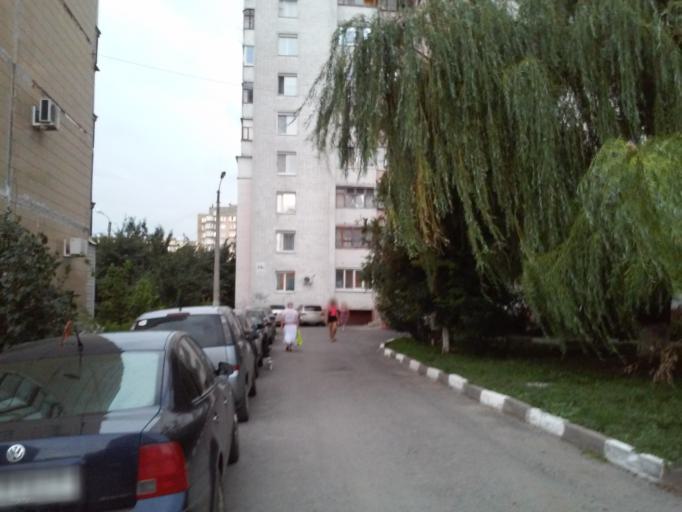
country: RU
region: Belgorod
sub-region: Belgorodskiy Rayon
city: Belgorod
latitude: 50.5681
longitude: 36.5734
